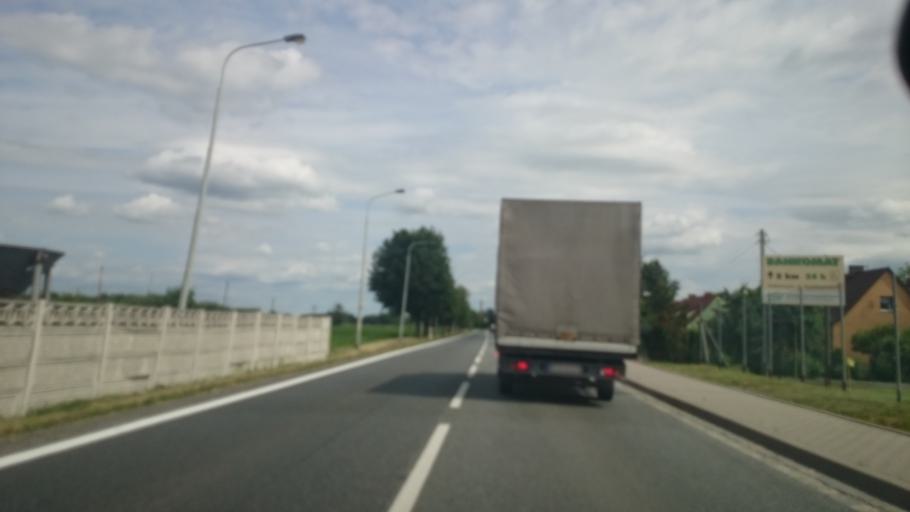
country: PL
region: Lower Silesian Voivodeship
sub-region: Powiat wroclawski
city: Jordanow Slaski
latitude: 50.9196
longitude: 16.8931
